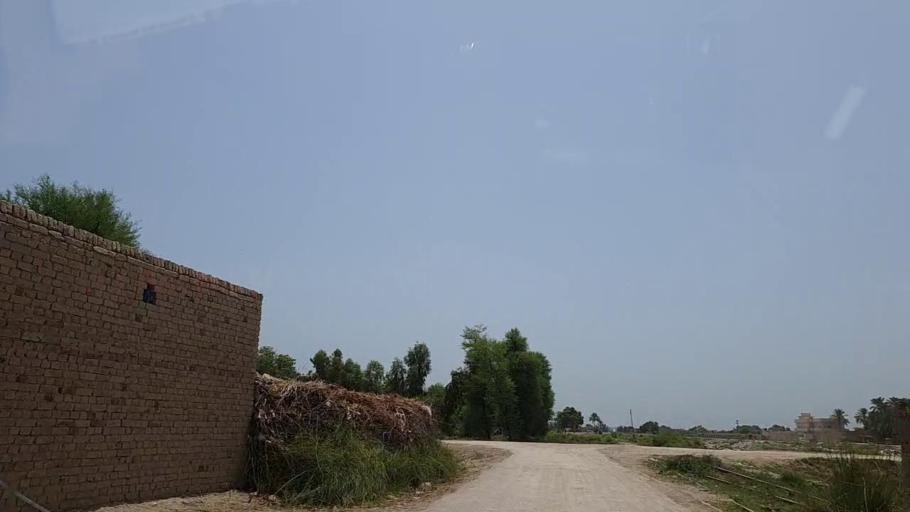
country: PK
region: Sindh
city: Tharu Shah
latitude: 26.9387
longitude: 68.1074
